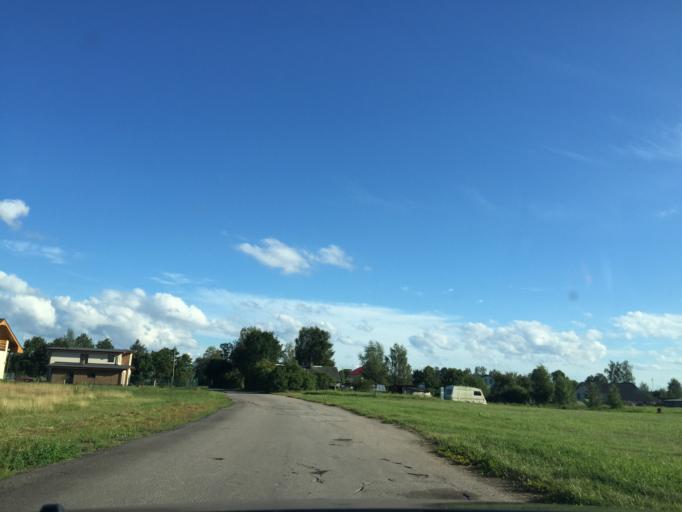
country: LV
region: Riga
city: Jaunciems
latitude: 57.0613
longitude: 24.1383
